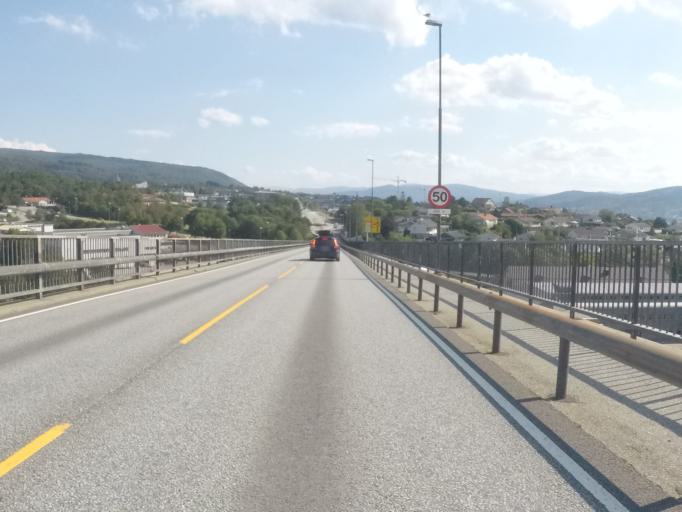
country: NO
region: Hordaland
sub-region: Lindas
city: Knarvik
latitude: 60.5440
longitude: 5.2763
